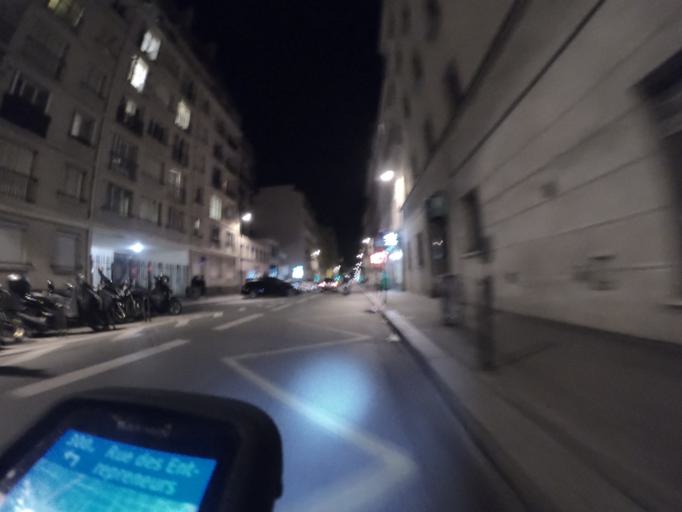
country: FR
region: Ile-de-France
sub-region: Departement des Hauts-de-Seine
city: Vanves
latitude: 48.8480
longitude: 2.2900
